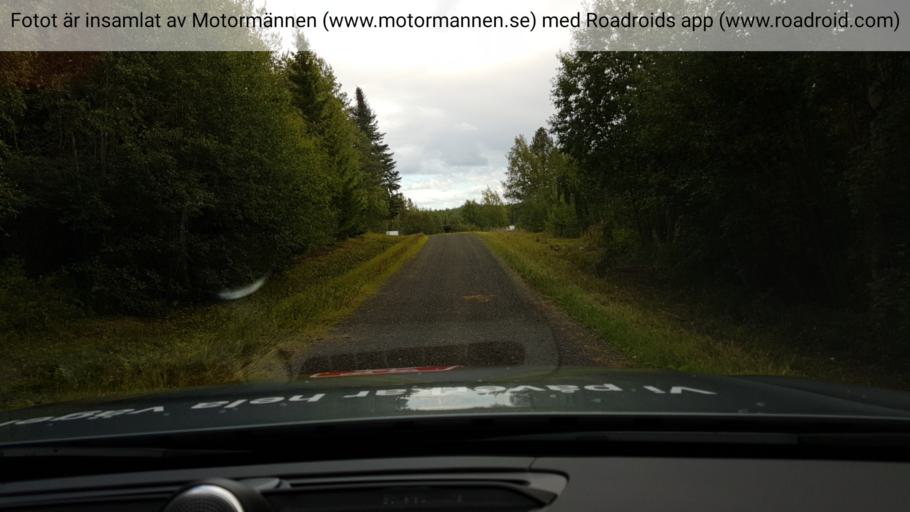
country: SE
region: Jaemtland
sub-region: Krokoms Kommun
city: Krokom
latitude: 63.7729
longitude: 14.6388
